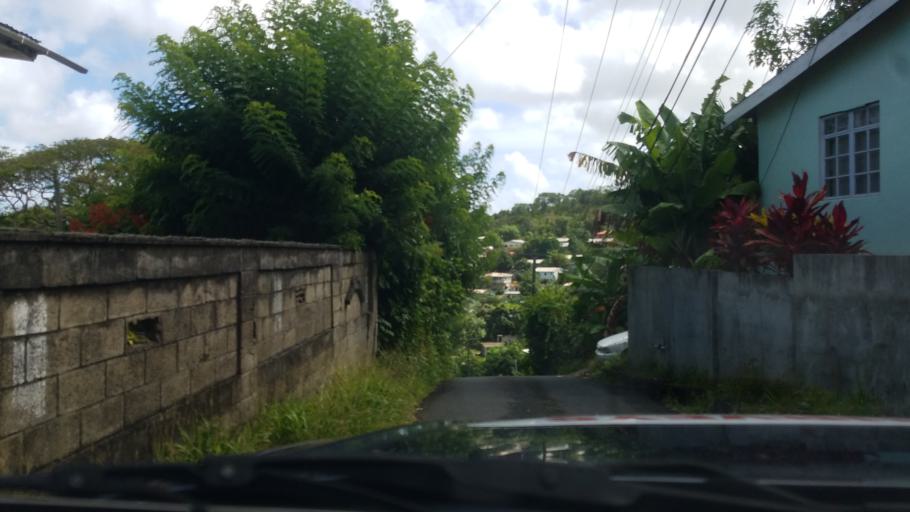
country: LC
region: Castries Quarter
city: Bisee
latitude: 14.0173
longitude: -60.9807
